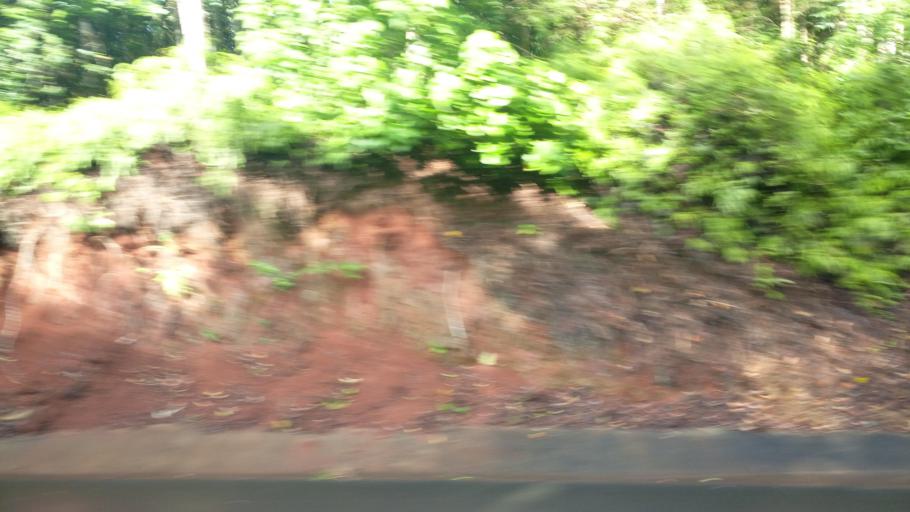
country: AU
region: Queensland
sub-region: Cassowary Coast
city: Innisfail
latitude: -17.4438
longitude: 145.9491
